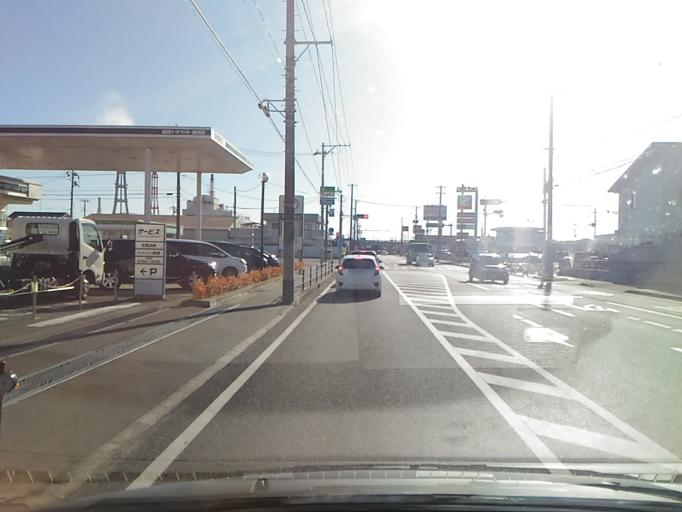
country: JP
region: Ibaraki
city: Kitaibaraki
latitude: 36.9191
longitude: 140.8033
